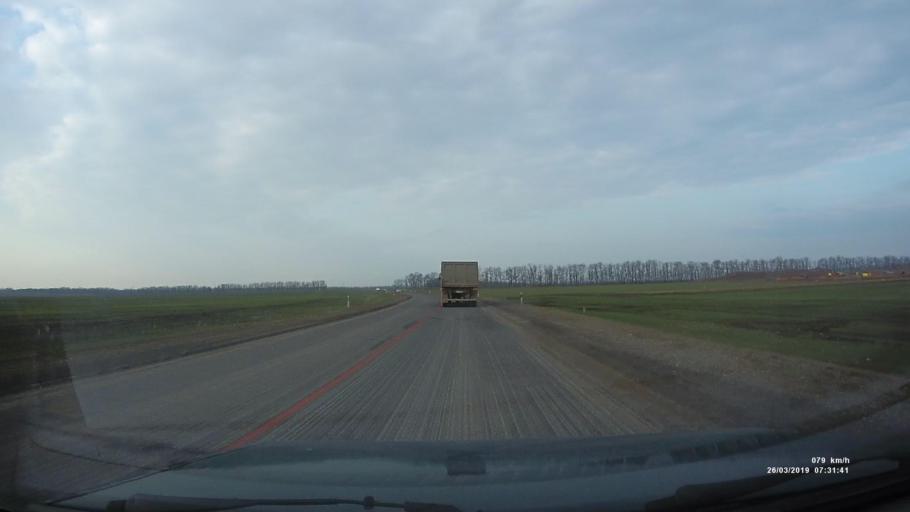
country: RU
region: Rostov
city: Novobessergenovka
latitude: 47.2317
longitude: 38.7872
